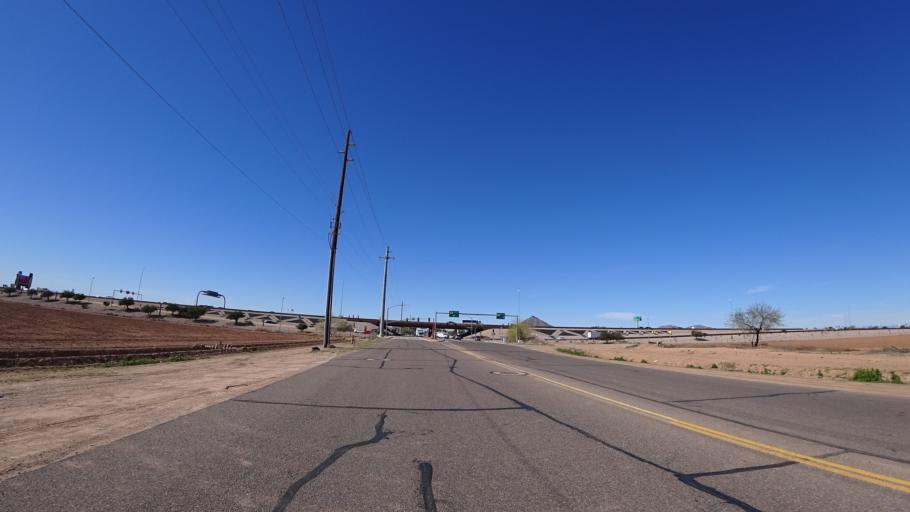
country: US
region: Arizona
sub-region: Maricopa County
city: Scottsdale
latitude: 33.4948
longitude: -111.8859
